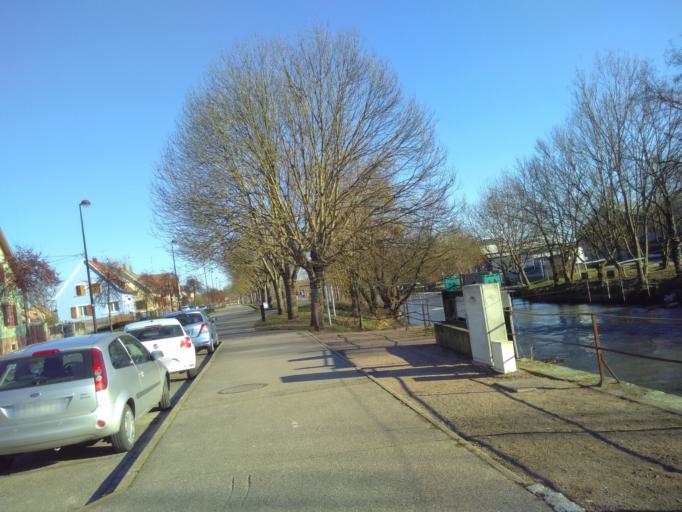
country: FR
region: Alsace
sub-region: Departement du Bas-Rhin
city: Selestat
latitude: 48.2564
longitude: 7.4582
